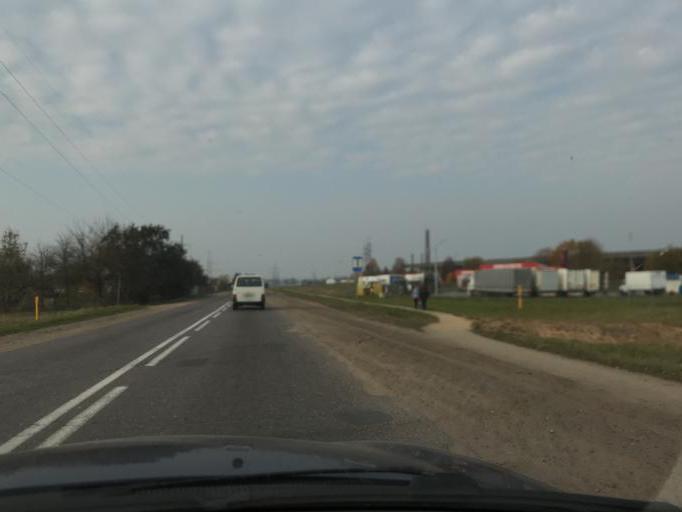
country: BY
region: Grodnenskaya
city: Lida
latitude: 53.8638
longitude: 25.2828
